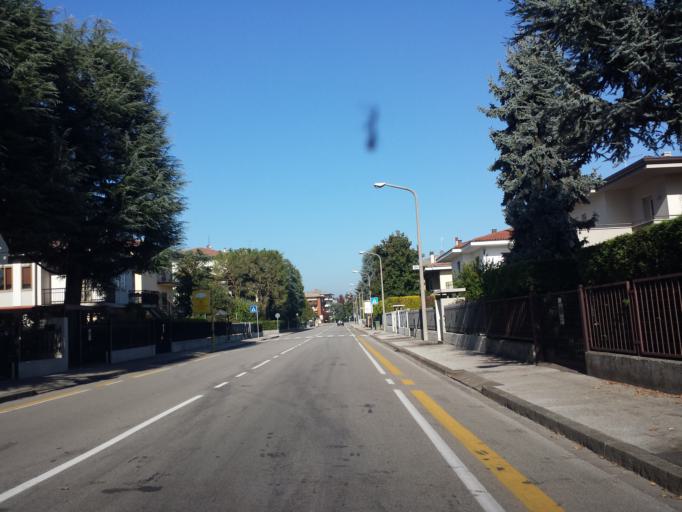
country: IT
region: Veneto
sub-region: Provincia di Vicenza
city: Vicenza
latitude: 45.5711
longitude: 11.5437
